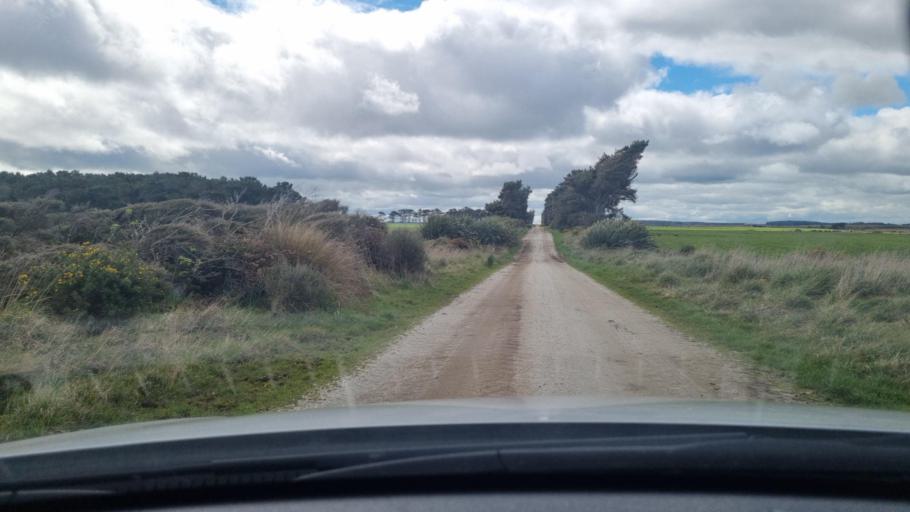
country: NZ
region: Southland
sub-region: Invercargill City
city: Bluff
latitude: -46.5722
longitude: 168.4979
